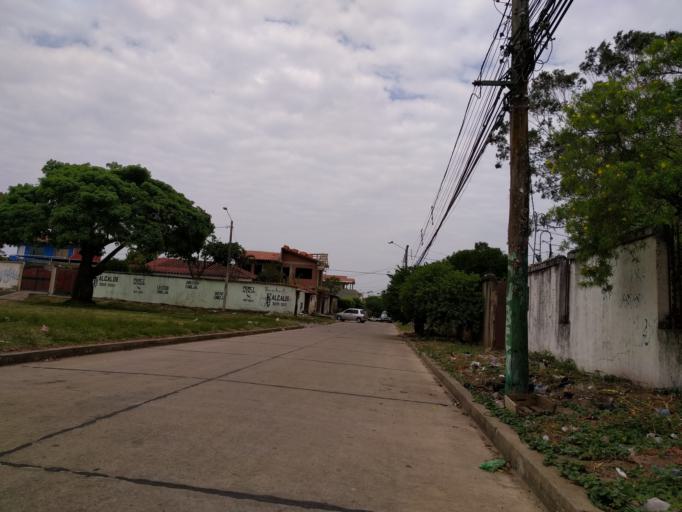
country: BO
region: Santa Cruz
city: Santa Cruz de la Sierra
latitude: -17.7942
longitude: -63.2095
